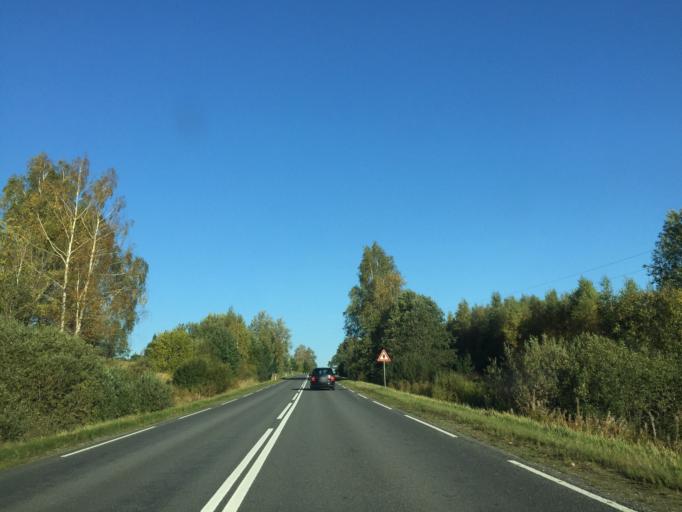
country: LV
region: Raunas
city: Rauna
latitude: 57.2203
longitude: 25.5868
